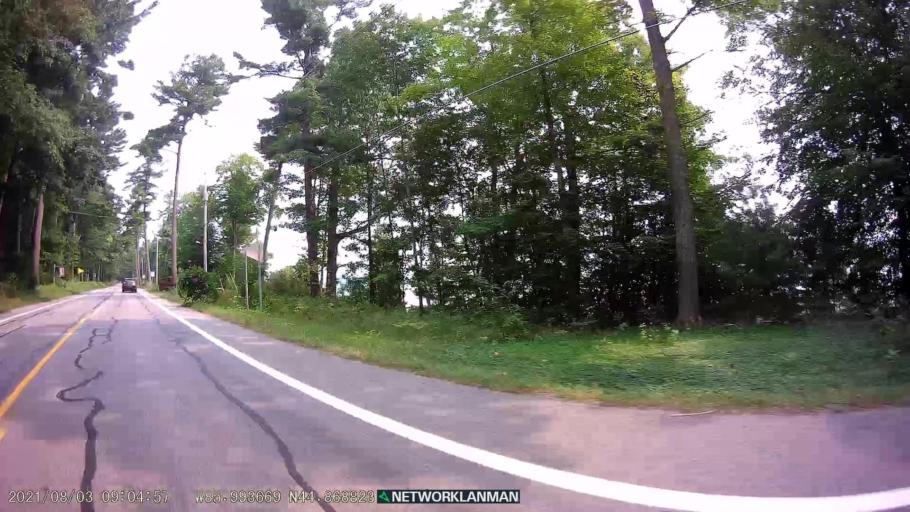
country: US
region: Michigan
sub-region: Benzie County
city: Beulah
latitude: 44.8688
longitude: -85.9938
